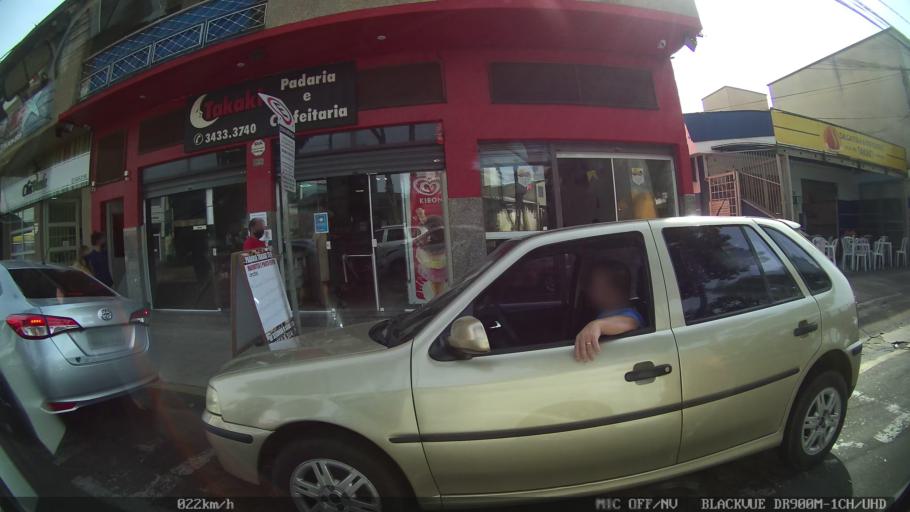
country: BR
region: Sao Paulo
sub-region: Piracicaba
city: Piracicaba
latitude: -22.7376
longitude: -47.6587
